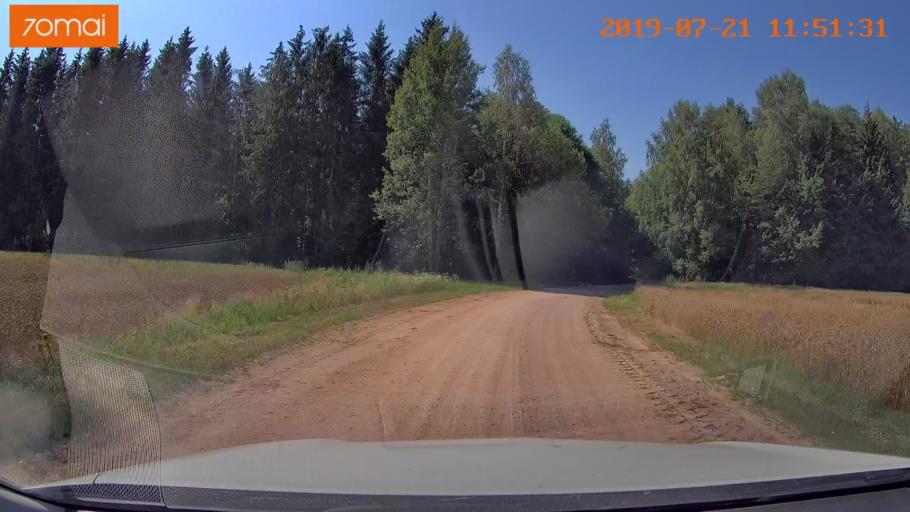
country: BY
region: Grodnenskaya
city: Lyubcha
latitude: 53.8828
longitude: 26.0122
